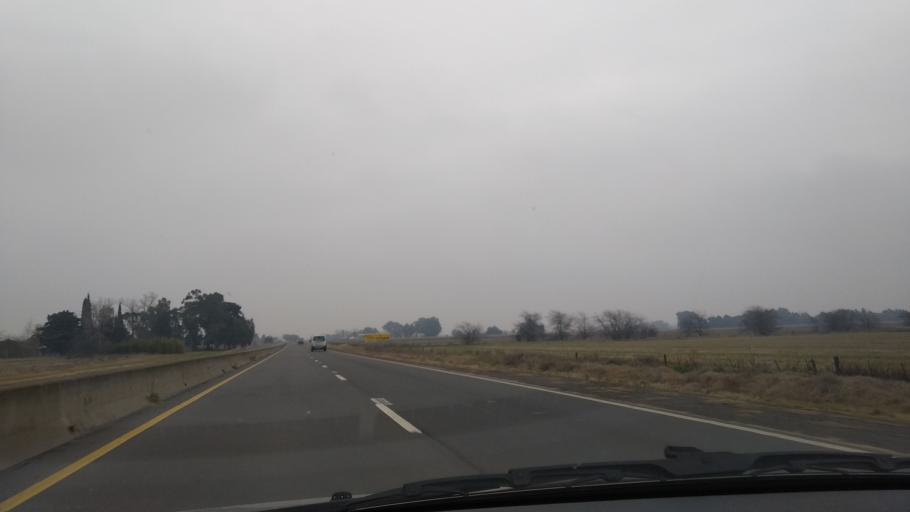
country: AR
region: Buenos Aires
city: Olavarria
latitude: -36.8722
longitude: -60.1361
